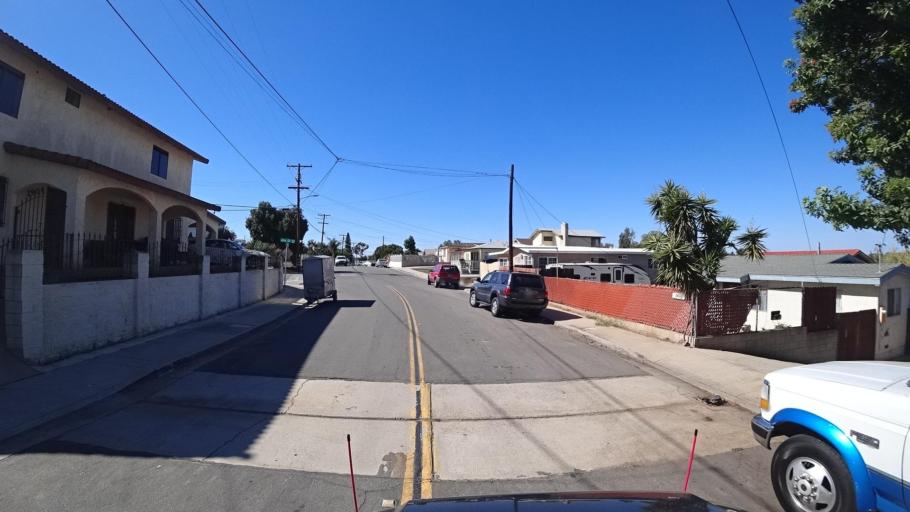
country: US
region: California
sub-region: San Diego County
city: Chula Vista
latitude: 32.6674
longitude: -117.0695
